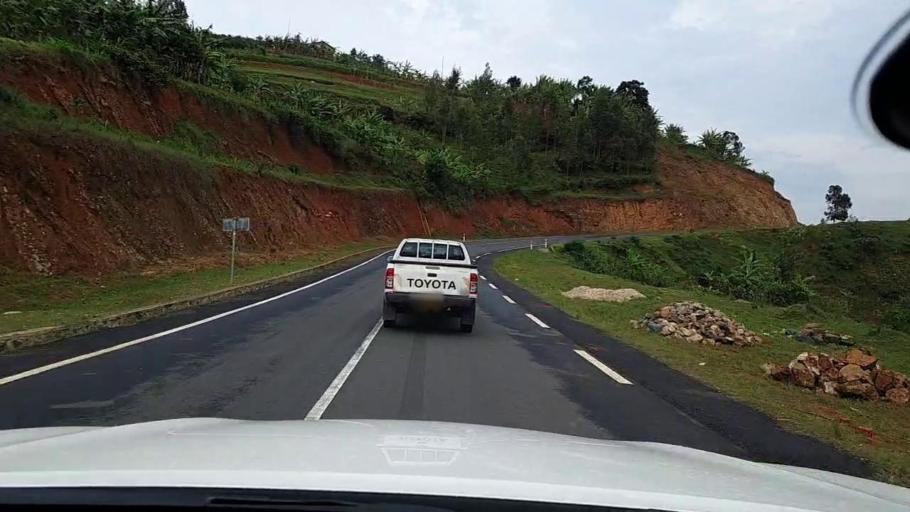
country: RW
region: Western Province
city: Kibuye
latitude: -2.1663
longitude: 29.2956
